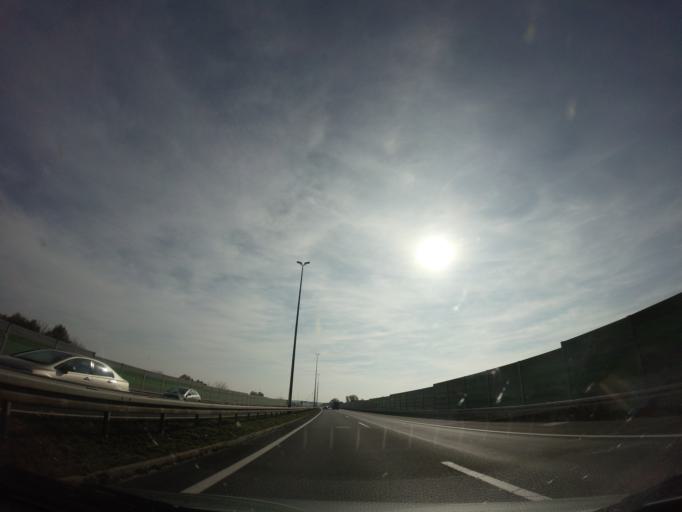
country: HR
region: Grad Zagreb
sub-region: Sesvete
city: Sesvete
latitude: 45.8278
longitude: 16.1370
